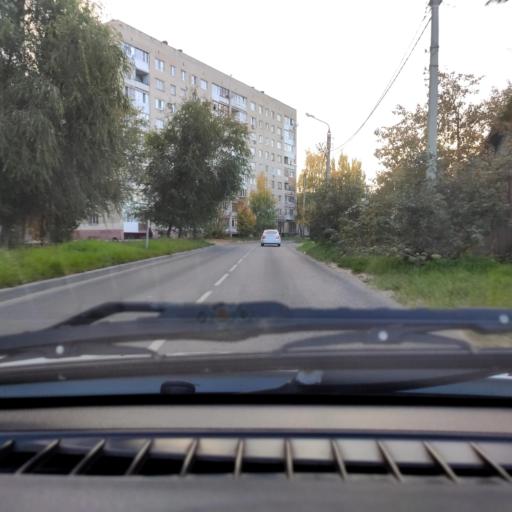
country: RU
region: Samara
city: Tol'yatti
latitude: 53.5077
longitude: 49.3984
